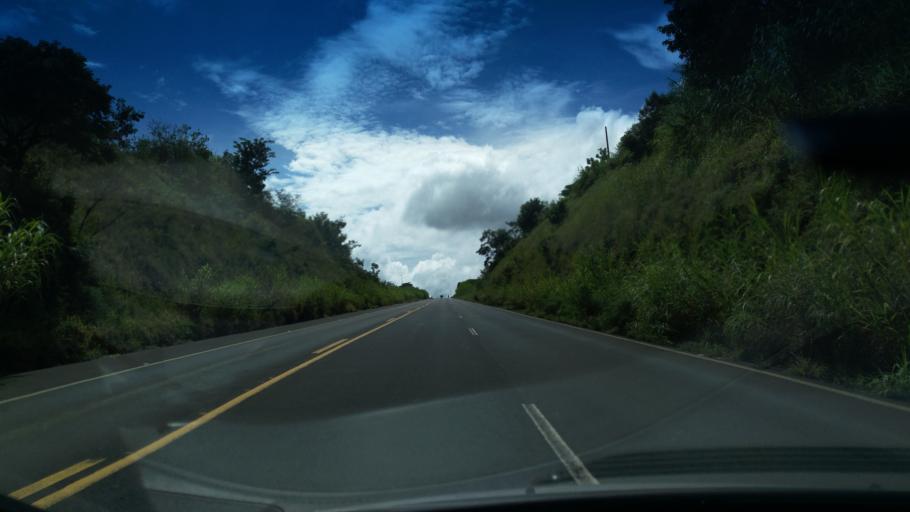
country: BR
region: Sao Paulo
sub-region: Santo Antonio Do Jardim
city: Espirito Santo do Pinhal
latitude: -22.1574
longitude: -46.7270
